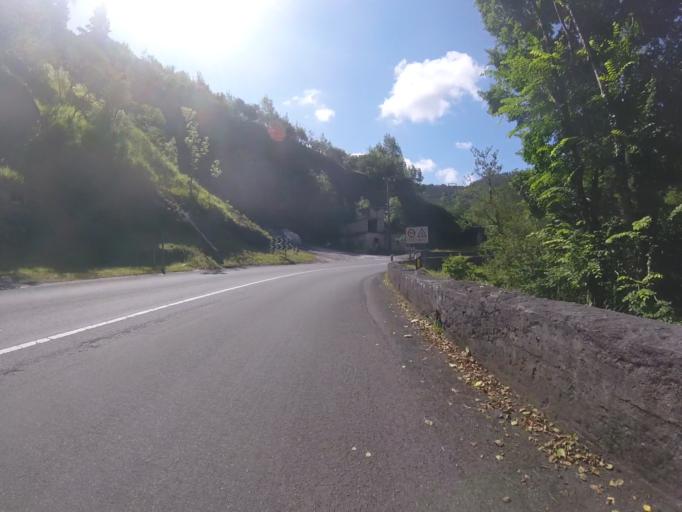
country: ES
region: Basque Country
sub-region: Provincia de Guipuzcoa
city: Azpeitia
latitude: 43.1778
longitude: -2.2238
